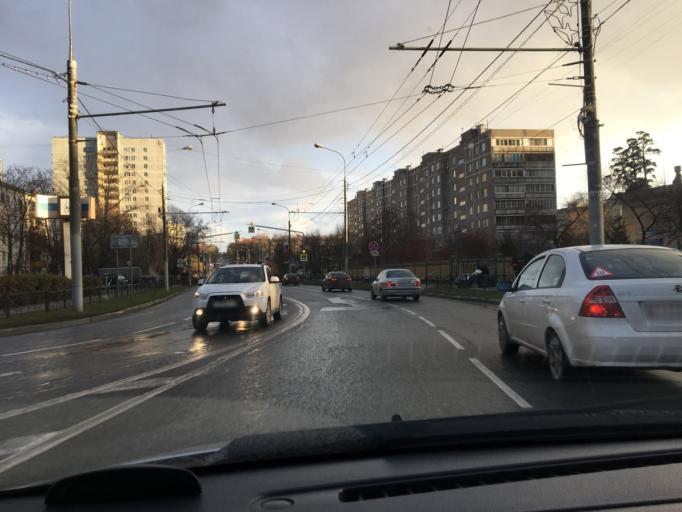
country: RU
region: Moskovskaya
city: Vidnoye
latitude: 55.5536
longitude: 37.6986
